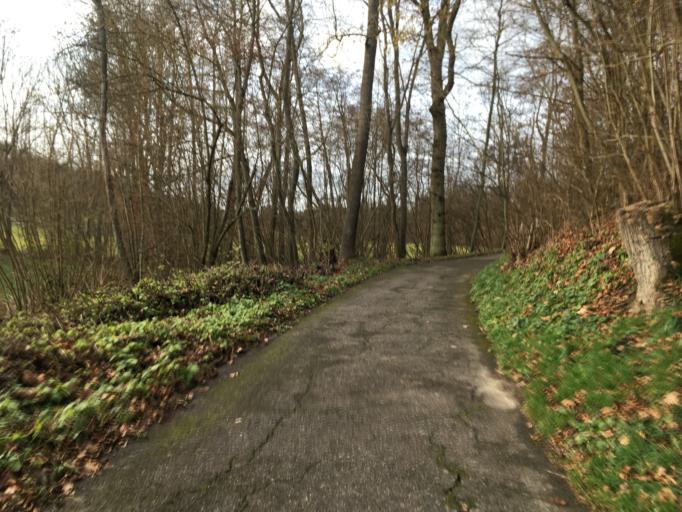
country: DE
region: Baden-Wuerttemberg
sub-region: Regierungsbezirk Stuttgart
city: Bad Wimpfen
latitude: 49.1997
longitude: 9.1383
